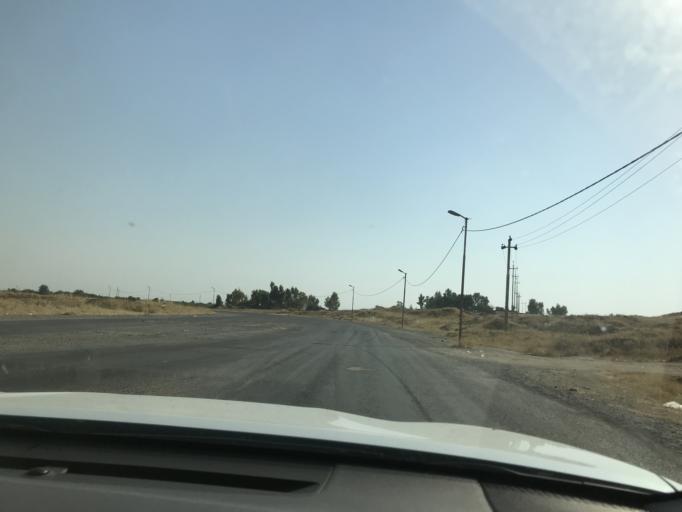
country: IQ
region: Arbil
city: Erbil
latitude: 36.1740
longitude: 43.9248
